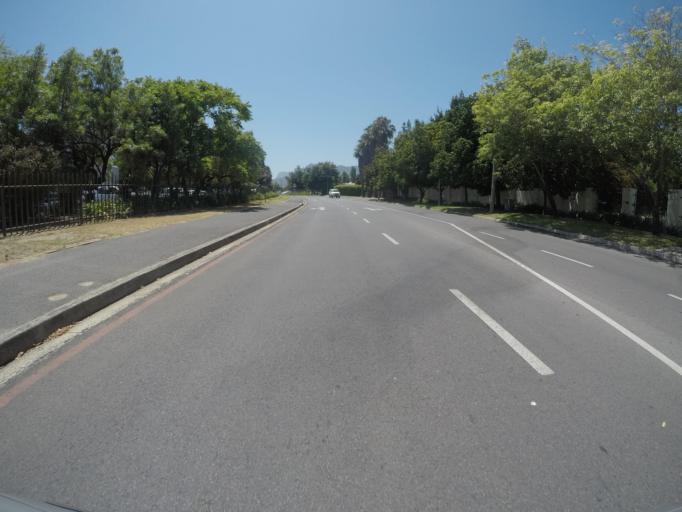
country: ZA
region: Western Cape
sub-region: Cape Winelands District Municipality
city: Stellenbosch
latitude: -33.9452
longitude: 18.8503
